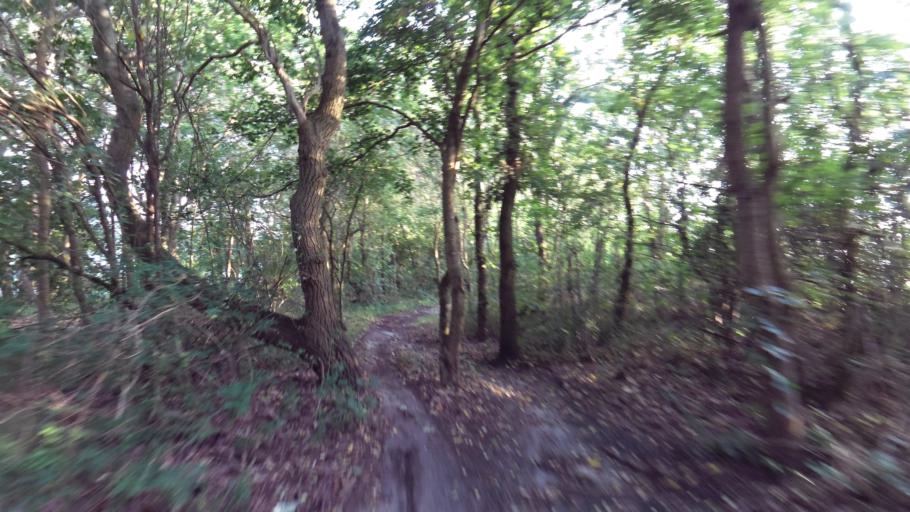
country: NL
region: South Holland
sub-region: Gemeente Noordwijkerhout
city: Noordwijkerhout
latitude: 52.2733
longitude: 4.4974
